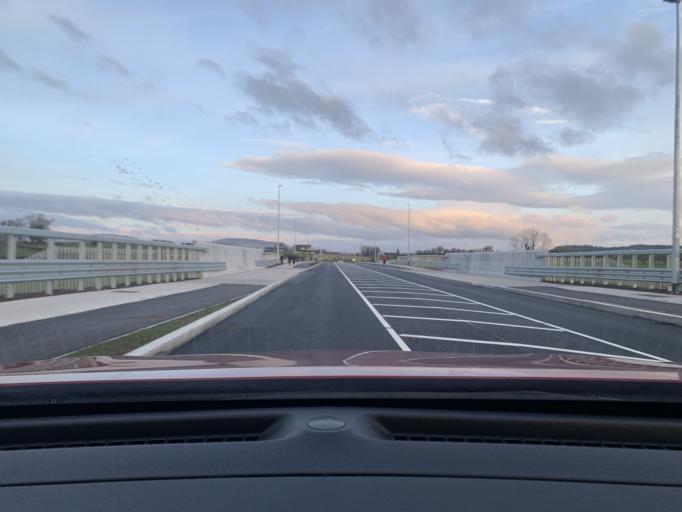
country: IE
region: Connaught
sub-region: Sligo
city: Sligo
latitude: 54.2599
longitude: -8.4927
